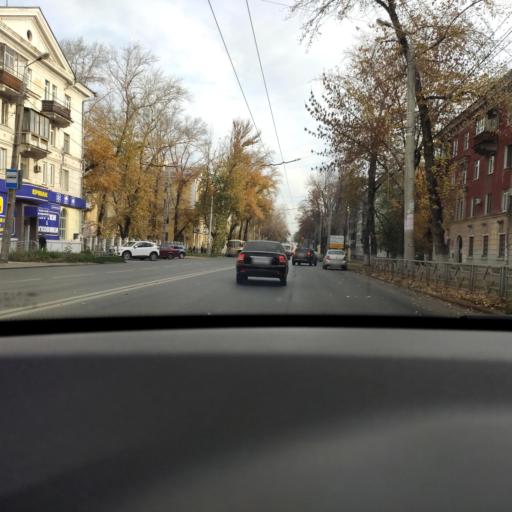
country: RU
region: Samara
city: Samara
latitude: 53.2262
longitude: 50.2611
